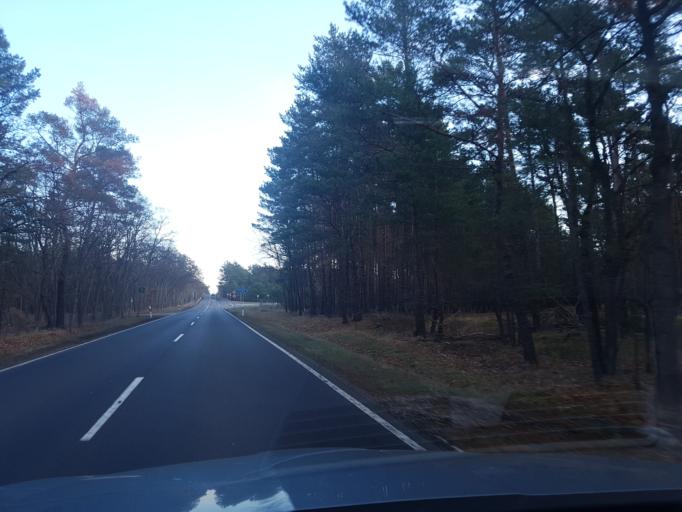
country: DE
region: Brandenburg
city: Kasel-Golzig
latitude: 52.0130
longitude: 13.6908
